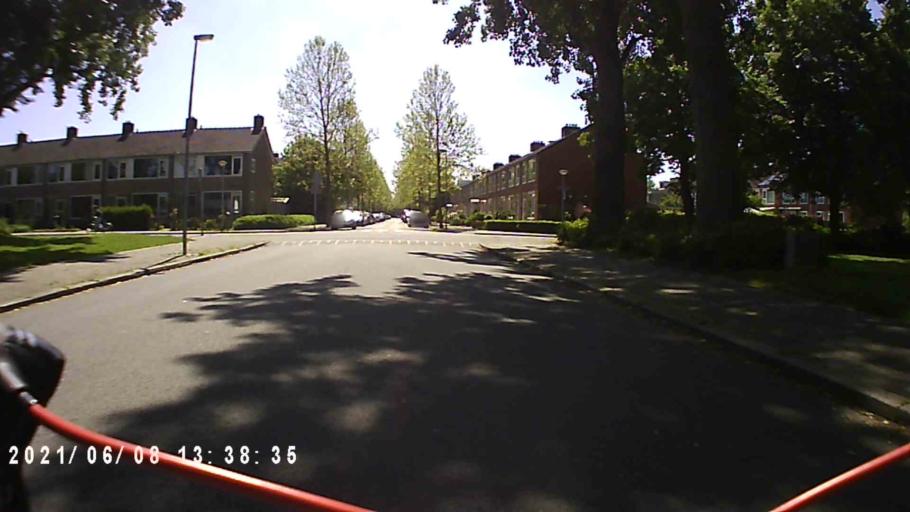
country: NL
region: Groningen
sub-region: Gemeente Groningen
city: Korrewegwijk
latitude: 53.2306
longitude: 6.5368
